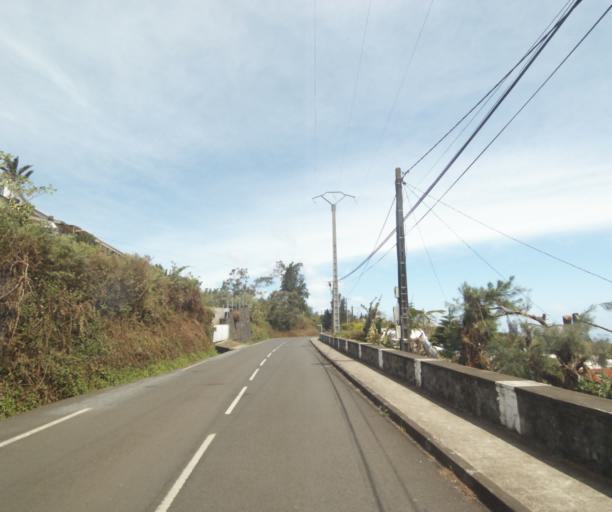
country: RE
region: Reunion
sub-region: Reunion
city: Trois-Bassins
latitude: -21.0598
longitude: 55.3080
